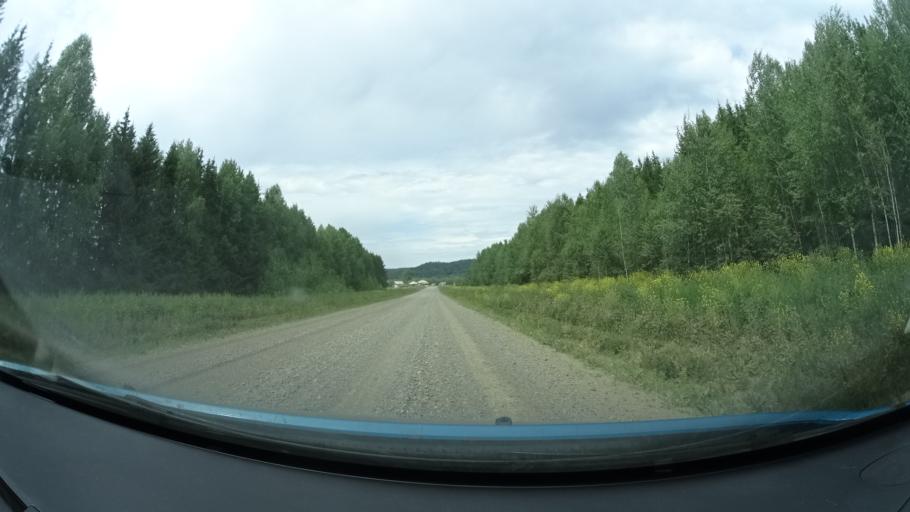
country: RU
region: Perm
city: Barda
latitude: 56.8065
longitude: 55.6741
